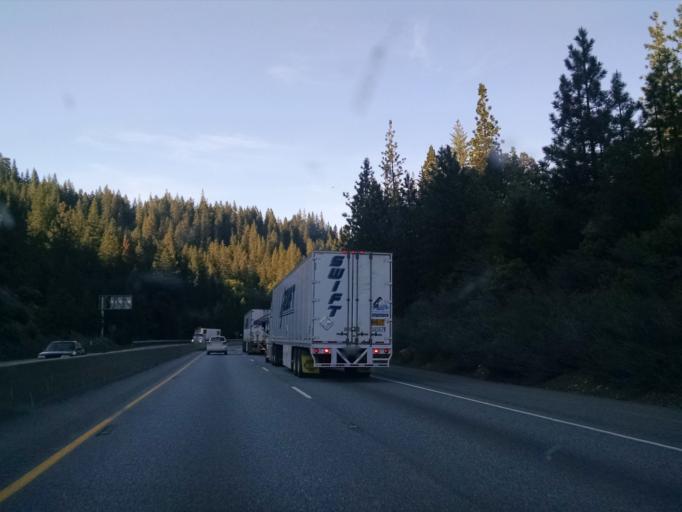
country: US
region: California
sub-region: Siskiyou County
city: Dunsmuir
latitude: 41.0791
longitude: -122.3560
